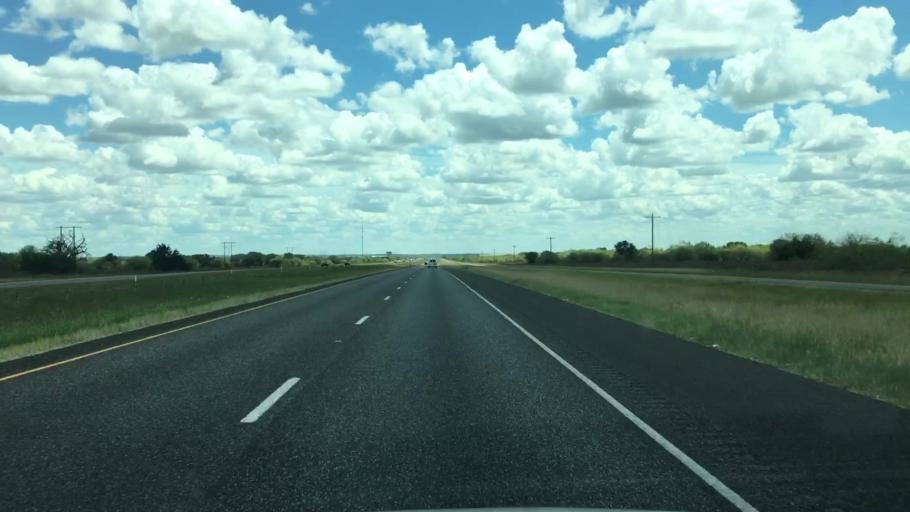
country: US
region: Texas
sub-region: Atascosa County
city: Pleasanton
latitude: 28.8154
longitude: -98.3568
